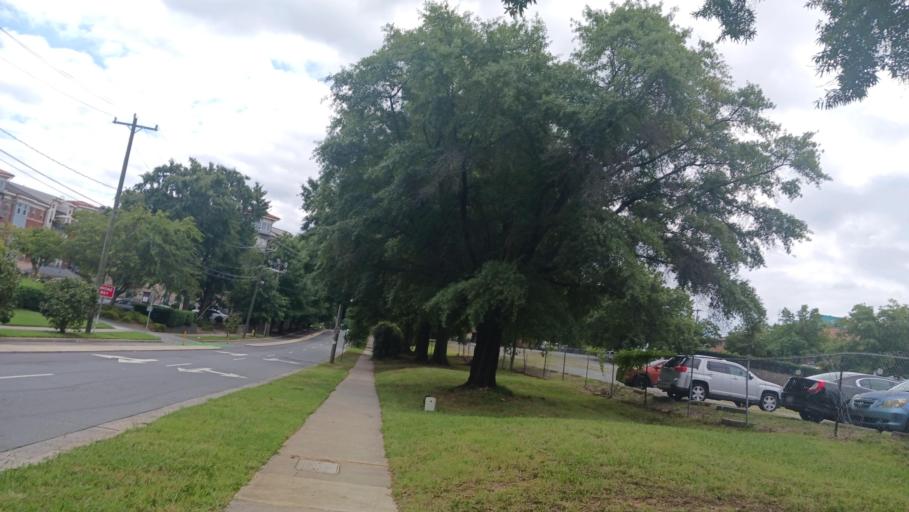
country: US
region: North Carolina
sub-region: Mecklenburg County
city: Charlotte
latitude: 35.2244
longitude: -80.8358
